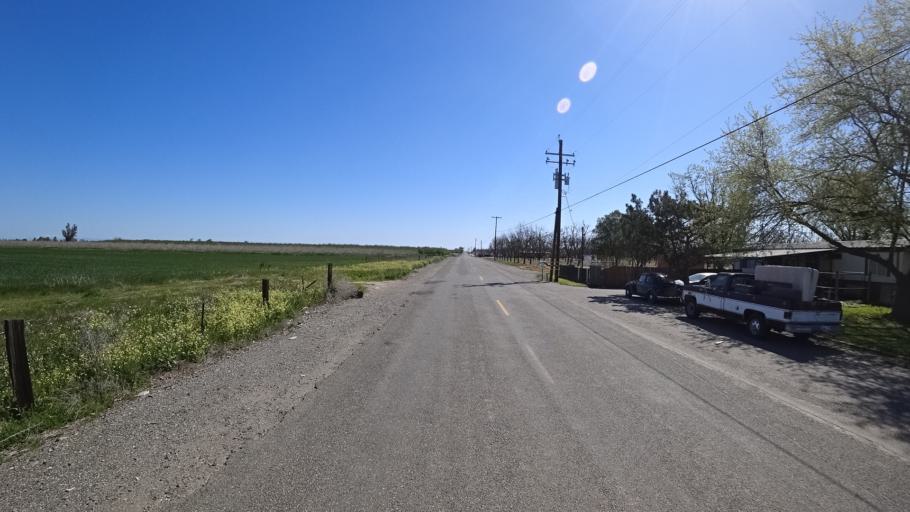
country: US
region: California
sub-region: Glenn County
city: Orland
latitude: 39.6971
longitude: -122.2187
